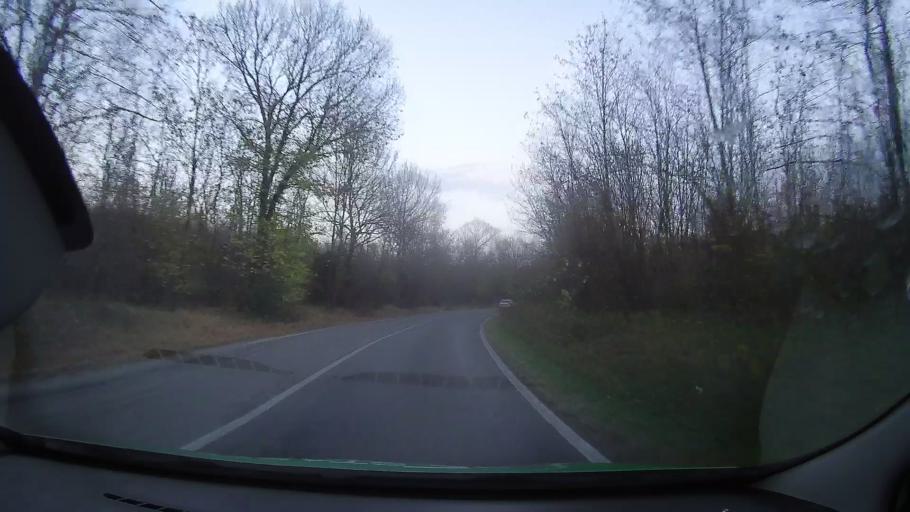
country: RO
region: Constanta
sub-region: Comuna Baneasa
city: Baneasa
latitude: 44.0871
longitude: 27.6646
